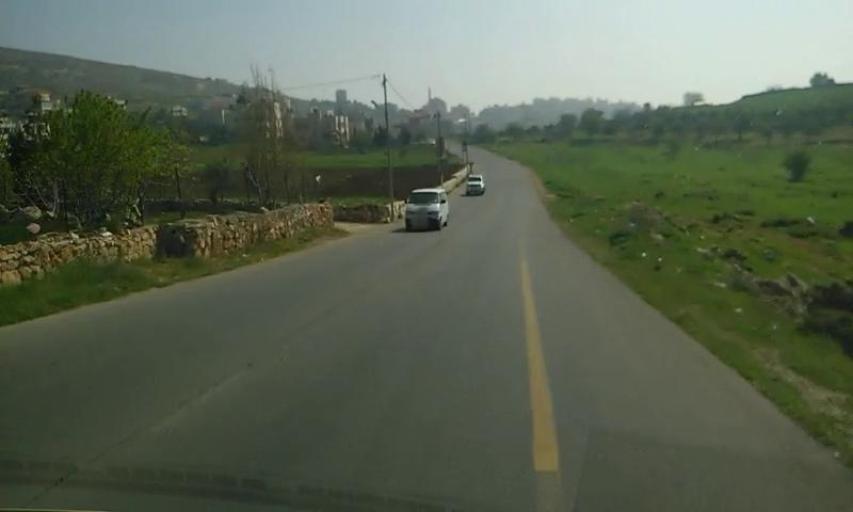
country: PS
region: West Bank
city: Dayr Jarir
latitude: 31.9706
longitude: 35.2807
